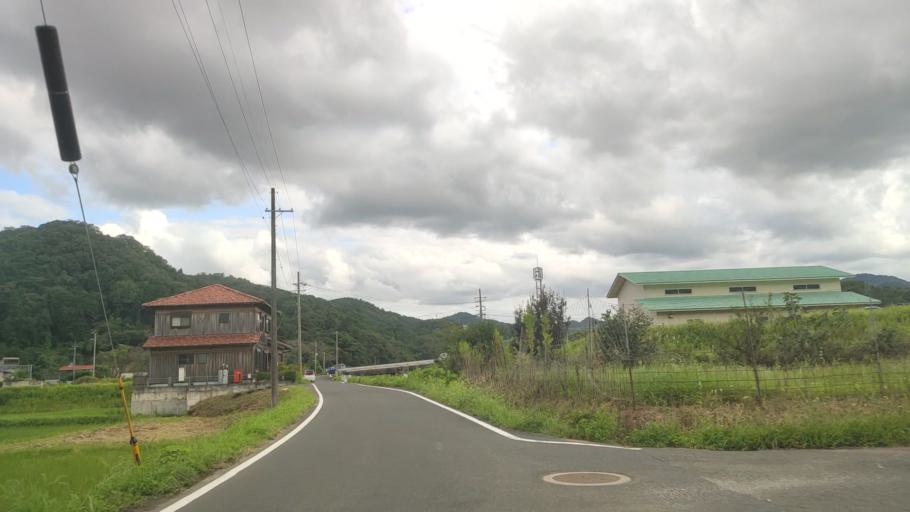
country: JP
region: Hyogo
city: Toyooka
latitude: 35.5974
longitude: 134.8854
